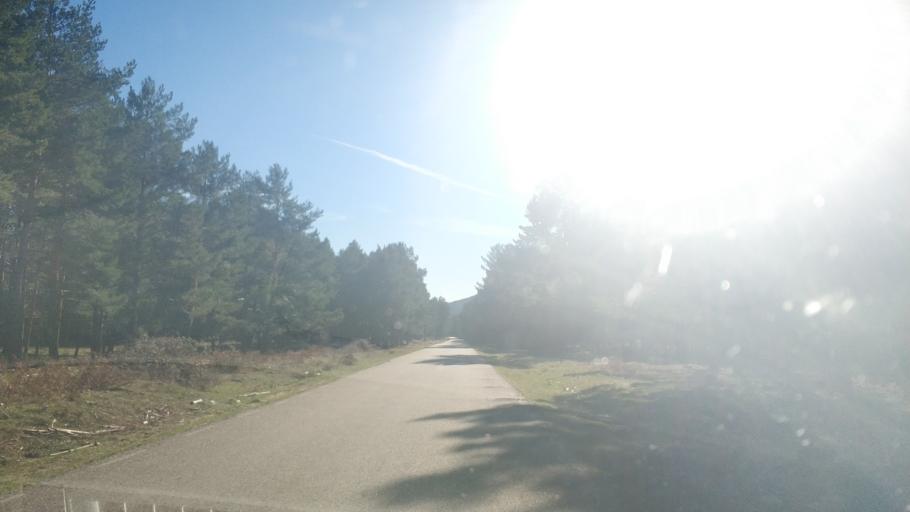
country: ES
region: Castille and Leon
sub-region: Provincia de Soria
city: Vinuesa
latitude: 41.9483
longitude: -2.7809
